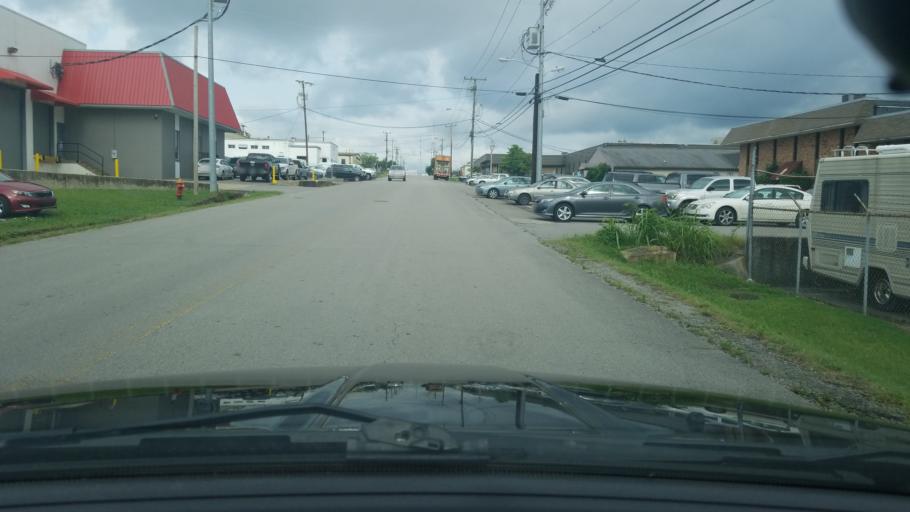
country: US
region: Tennessee
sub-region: Davidson County
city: Oak Hill
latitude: 36.0925
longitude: -86.7411
